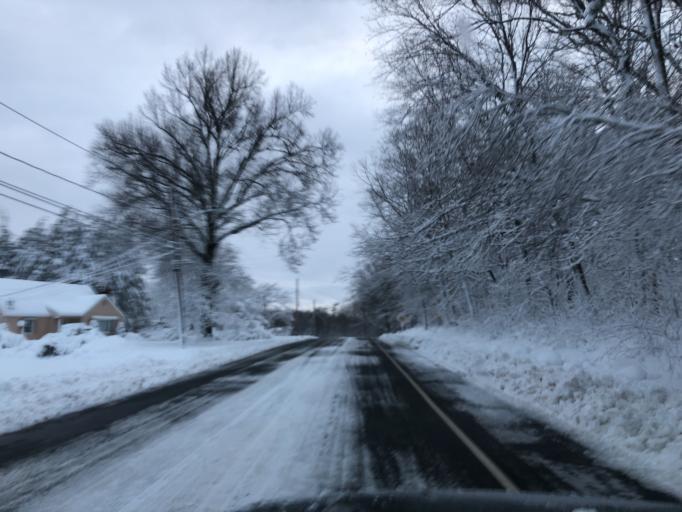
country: US
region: Connecticut
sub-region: Hartford County
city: New Britain
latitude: 41.6936
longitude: -72.7846
